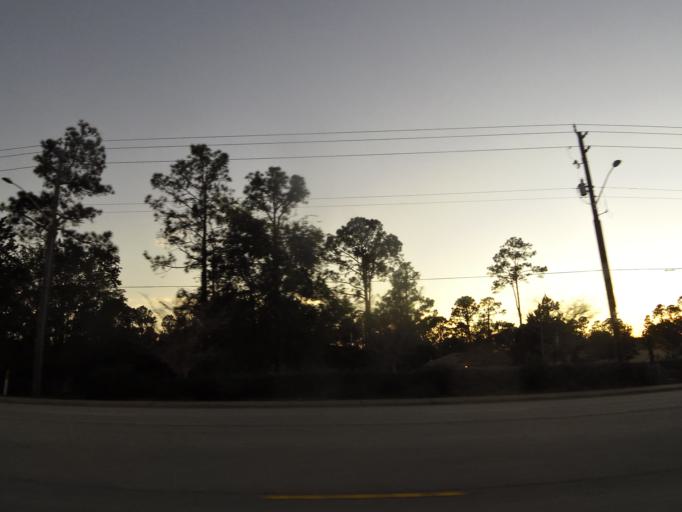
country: US
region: Florida
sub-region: Flagler County
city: Palm Coast
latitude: 29.5632
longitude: -81.2413
